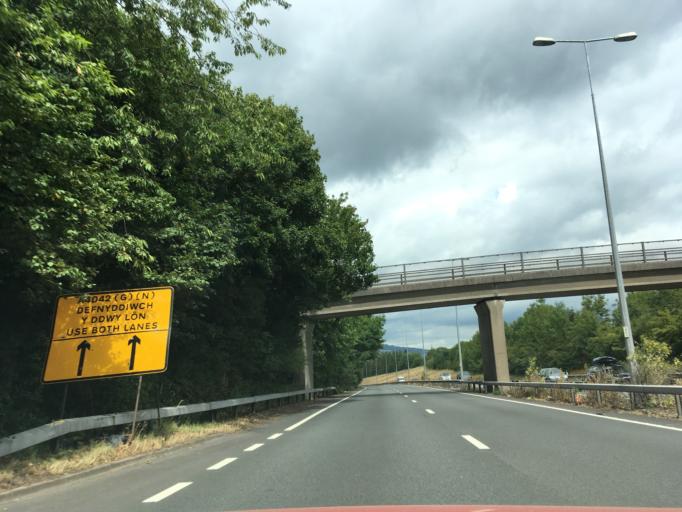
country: GB
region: Wales
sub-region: Torfaen County Borough
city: New Inn
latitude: 51.6723
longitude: -3.0077
